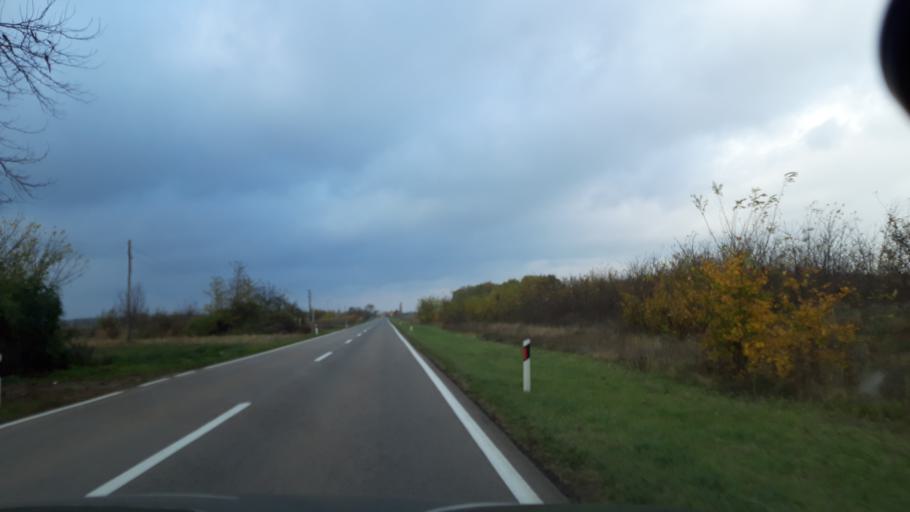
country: RS
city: Sanad
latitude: 45.9718
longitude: 20.1217
